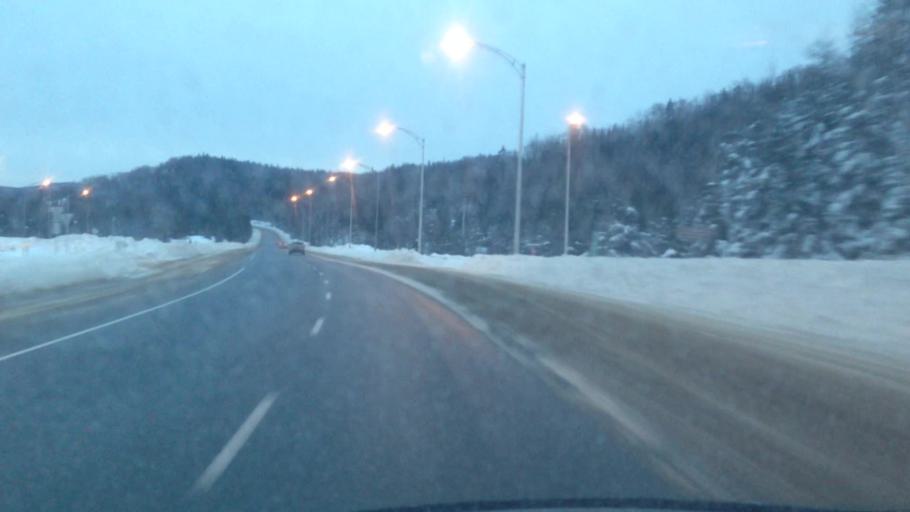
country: CA
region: Quebec
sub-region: Laurentides
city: Sainte-Agathe-des-Monts
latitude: 46.1186
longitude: -74.4321
